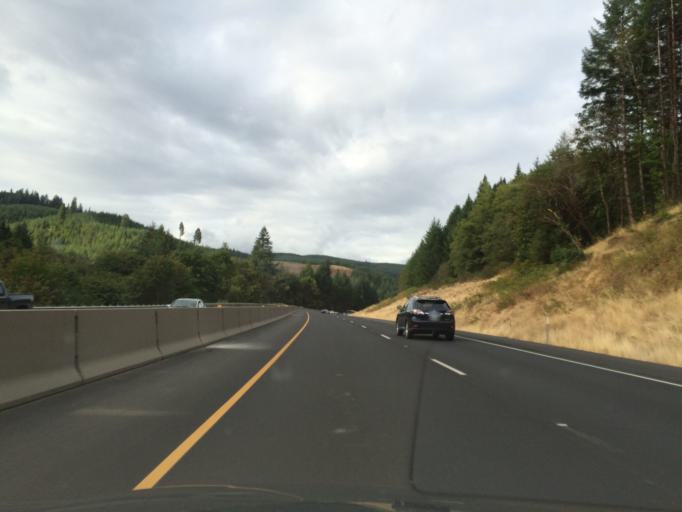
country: US
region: Oregon
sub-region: Lane County
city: Cottage Grove
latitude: 43.7430
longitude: -123.1823
